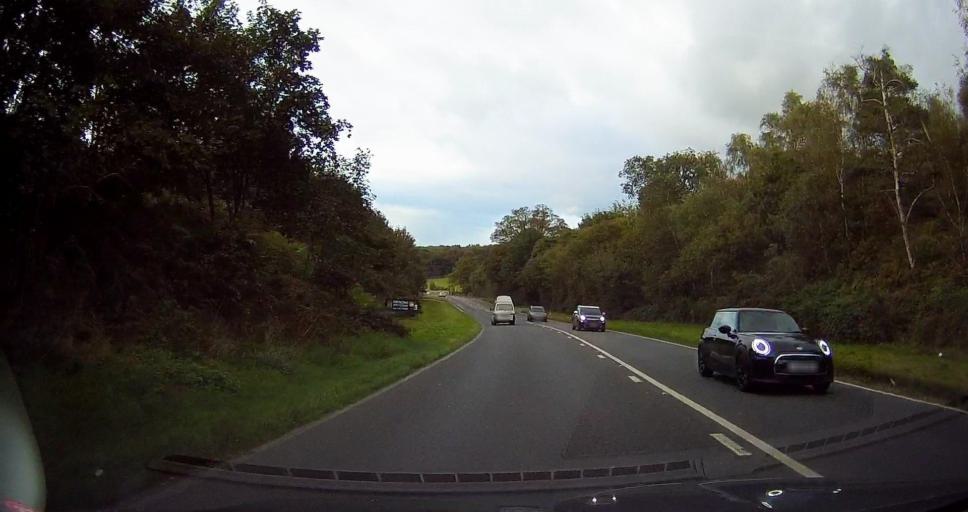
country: GB
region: England
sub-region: Kent
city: Harrietsham
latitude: 51.2512
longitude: 0.6355
